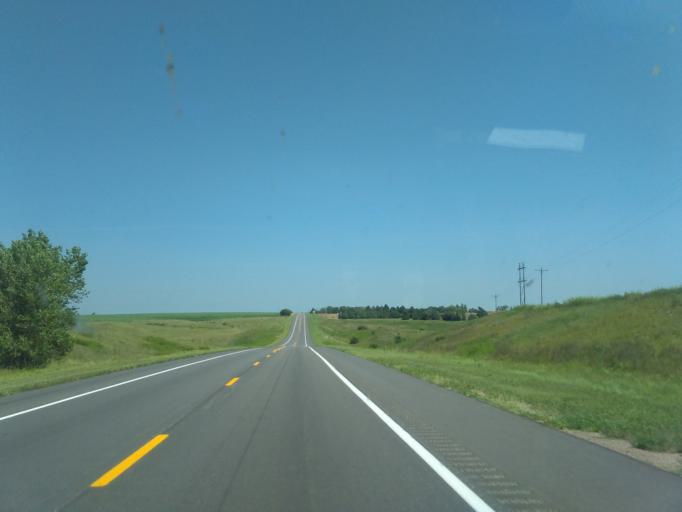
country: US
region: Nebraska
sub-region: Red Willow County
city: McCook
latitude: 40.2906
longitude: -100.6498
